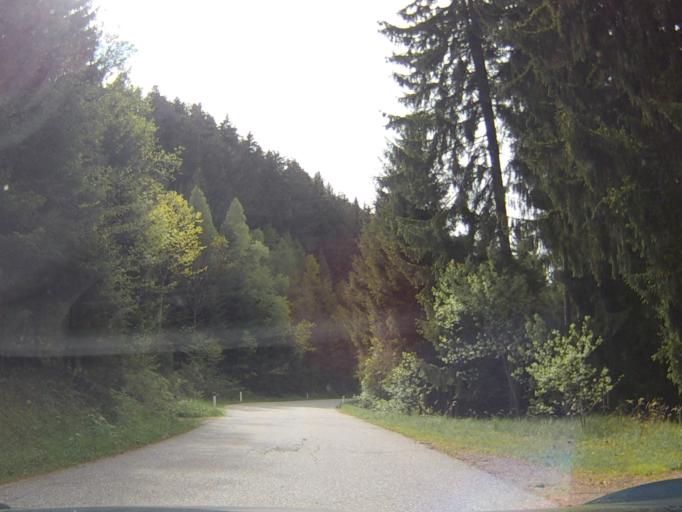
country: AT
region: Carinthia
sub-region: Politischer Bezirk Villach Land
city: Stockenboi
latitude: 46.7349
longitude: 13.5746
